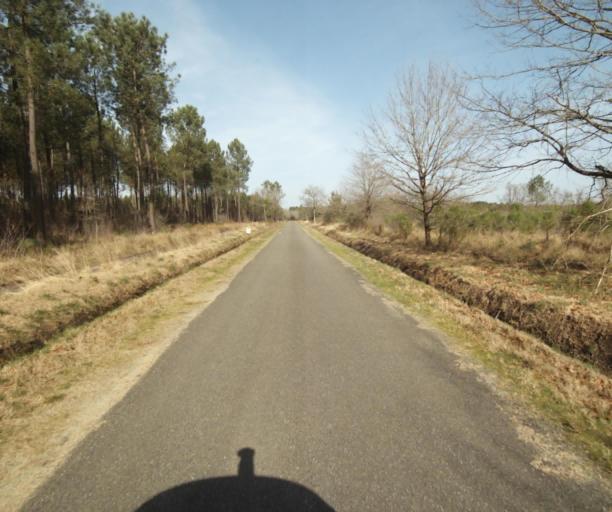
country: FR
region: Aquitaine
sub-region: Departement de la Gironde
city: Bazas
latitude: 44.2285
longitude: -0.2033
